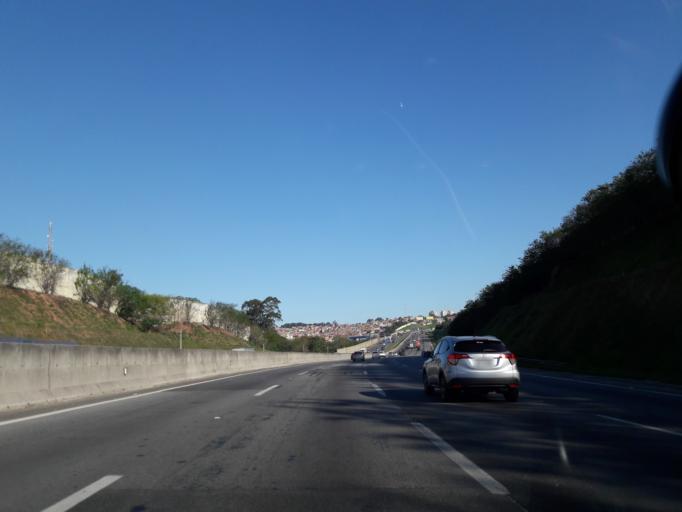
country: BR
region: Sao Paulo
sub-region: Osasco
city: Osasco
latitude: -23.5700
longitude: -46.8134
